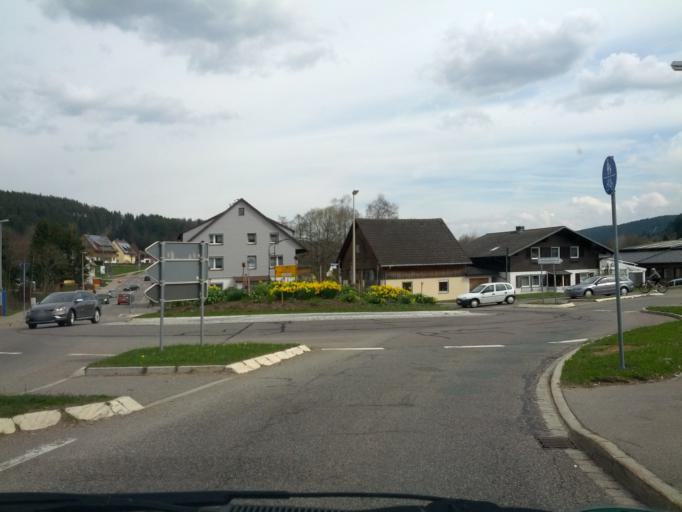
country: DE
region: Baden-Wuerttemberg
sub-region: Freiburg Region
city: Titisee-Neustadt
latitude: 47.9239
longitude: 8.1906
